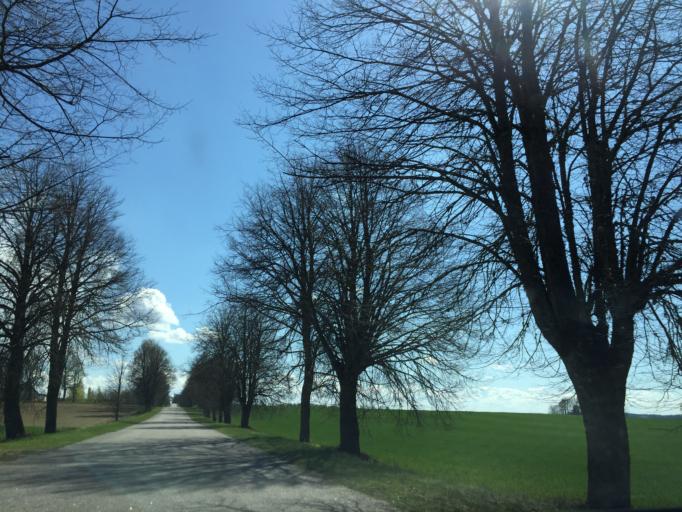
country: LV
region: Strenci
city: Strenci
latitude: 57.5574
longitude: 25.7130
